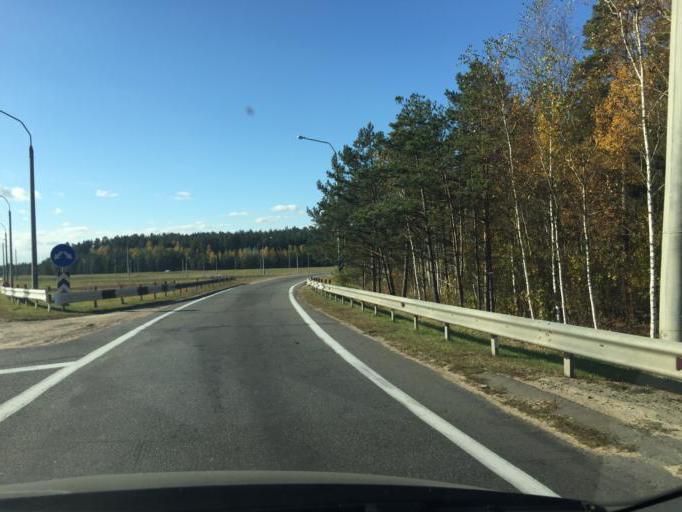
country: BY
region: Minsk
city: Slabada
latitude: 53.9512
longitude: 27.9813
